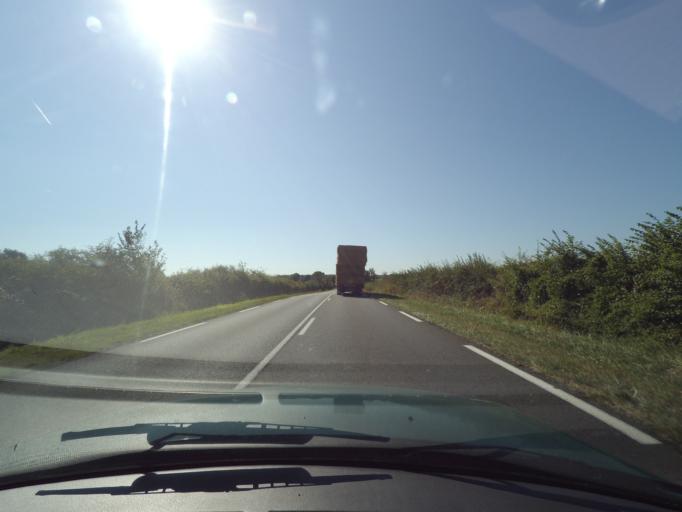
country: FR
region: Poitou-Charentes
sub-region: Departement de la Vienne
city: Lussac-les-Chateaux
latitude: 46.3772
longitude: 0.7555
